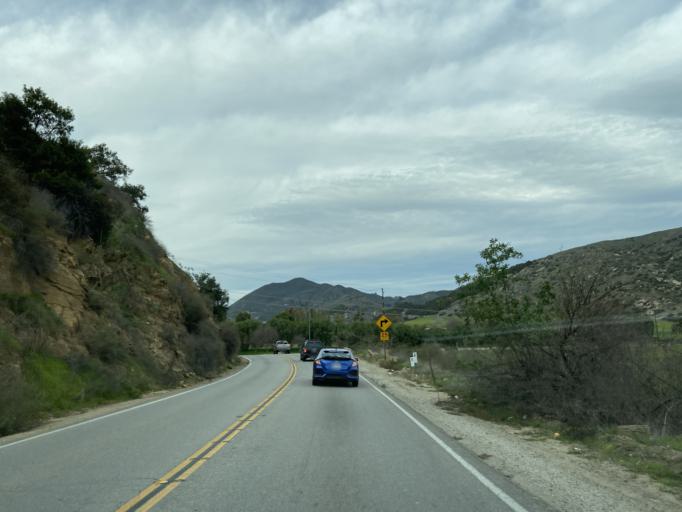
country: US
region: California
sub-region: San Diego County
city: Rainbow
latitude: 33.3419
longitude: -117.1329
